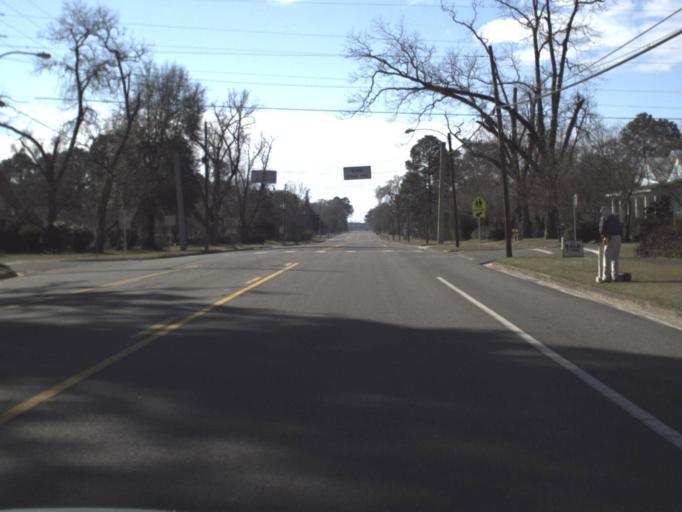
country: US
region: Florida
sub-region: Jackson County
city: Malone
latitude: 30.9539
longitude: -85.1627
